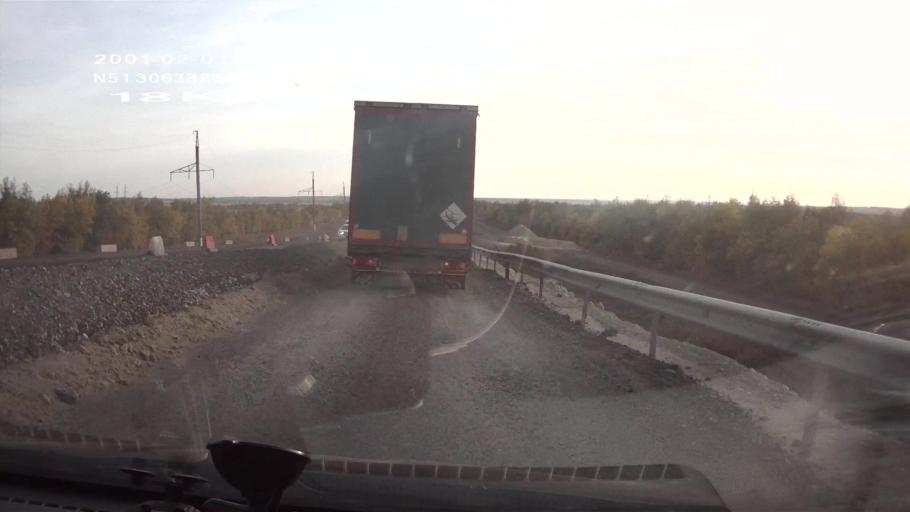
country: RU
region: Saratov
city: Krasnyy Oktyabr'
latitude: 51.3061
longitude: 45.6942
